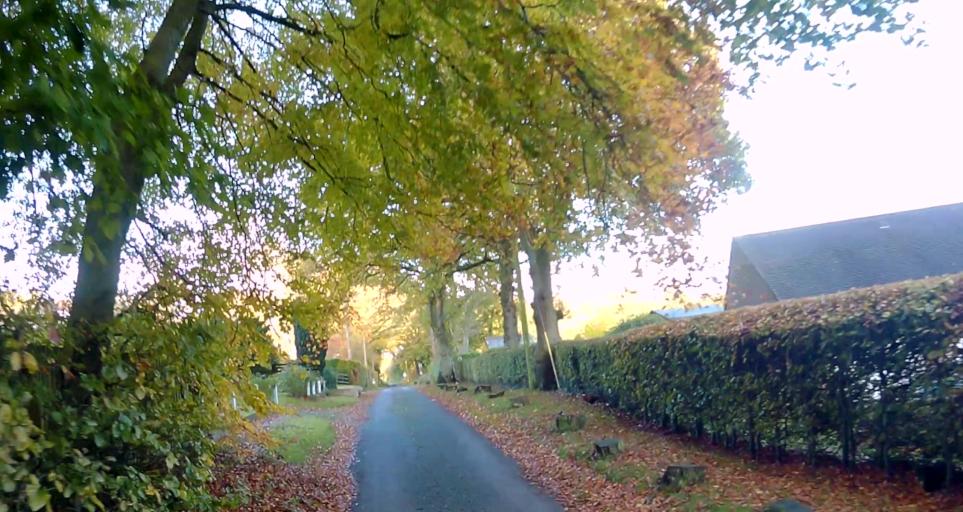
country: GB
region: England
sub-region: Hampshire
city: Basingstoke
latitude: 51.1920
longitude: -1.0920
